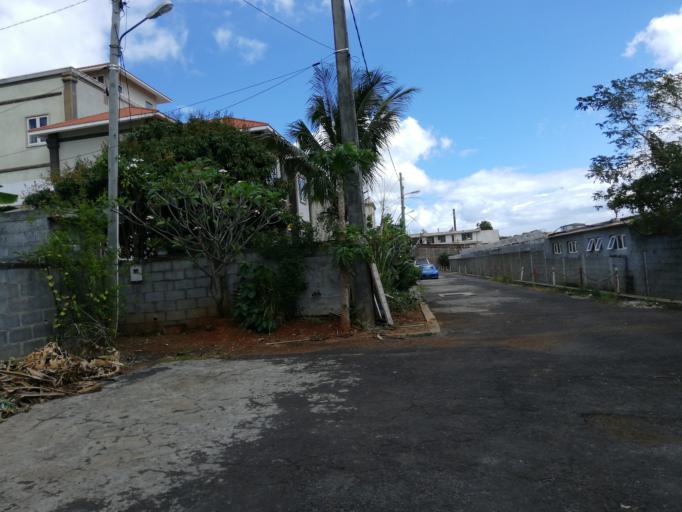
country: MU
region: Moka
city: Pailles
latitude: -20.2116
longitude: 57.4718
